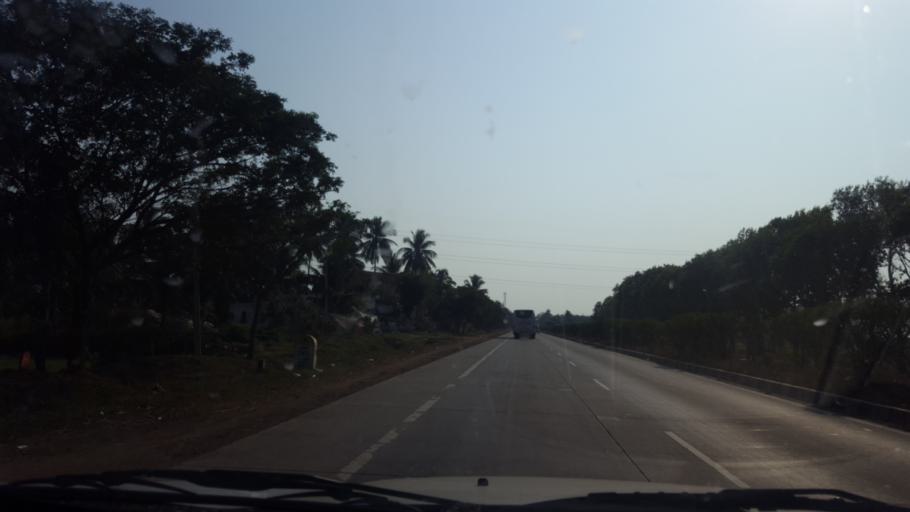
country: IN
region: Andhra Pradesh
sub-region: Vishakhapatnam
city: Etikoppaka
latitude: 17.4822
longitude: 82.7846
